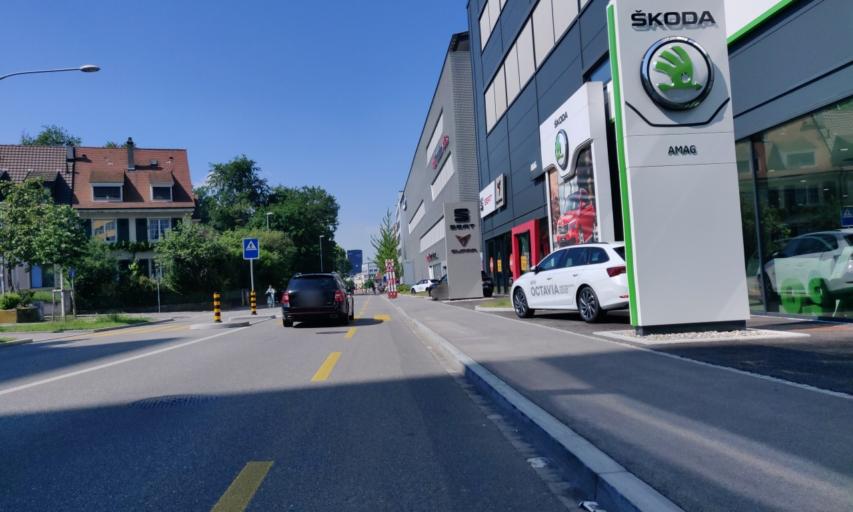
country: CH
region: Basel-Landschaft
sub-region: Bezirk Arlesheim
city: Munchenstein
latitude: 47.5338
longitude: 7.6050
